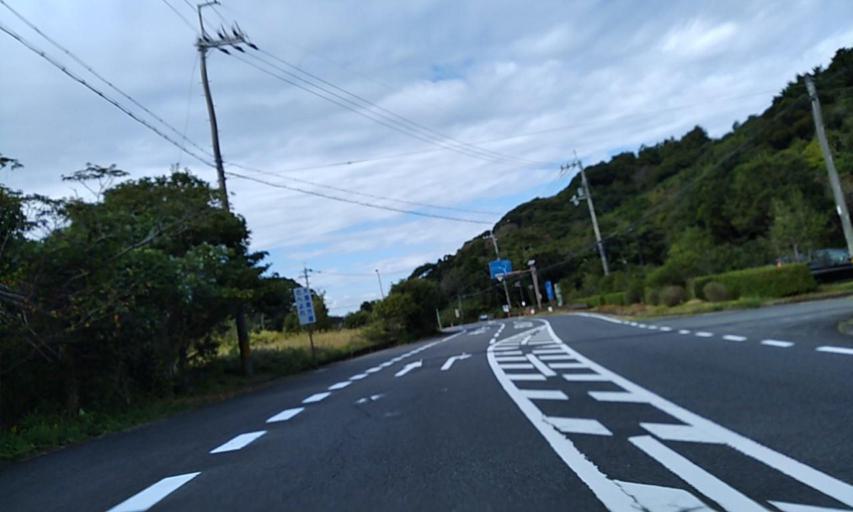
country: JP
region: Wakayama
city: Shingu
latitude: 33.4717
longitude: 135.8176
